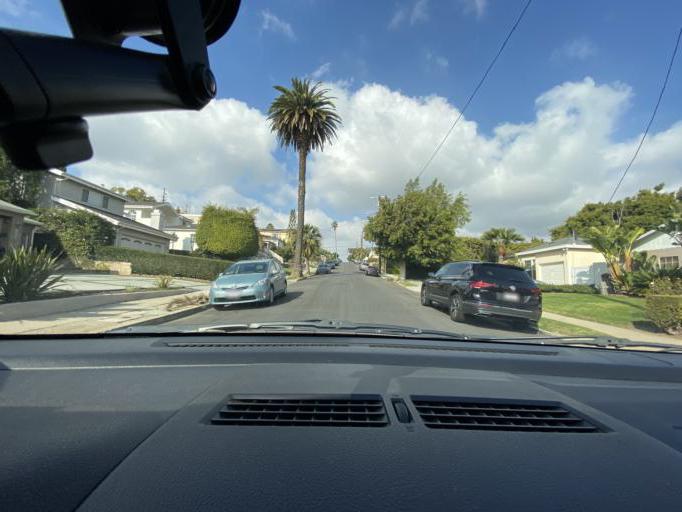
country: US
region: California
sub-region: Los Angeles County
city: Culver City
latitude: 34.0163
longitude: -118.4180
